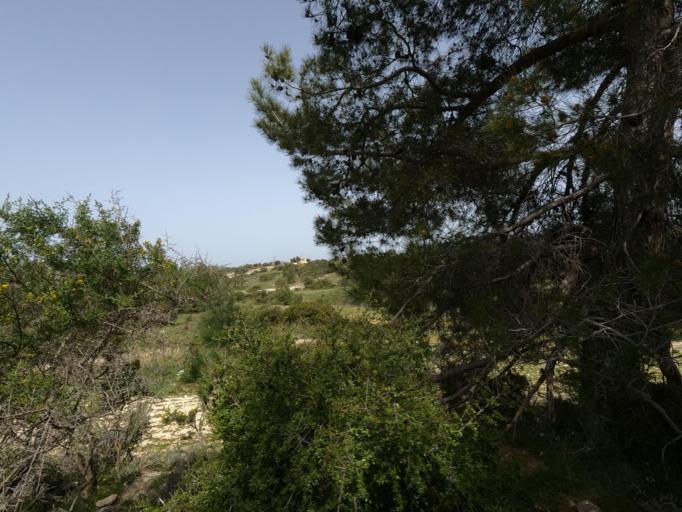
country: CY
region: Pafos
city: Polis
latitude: 35.0110
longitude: 32.3654
